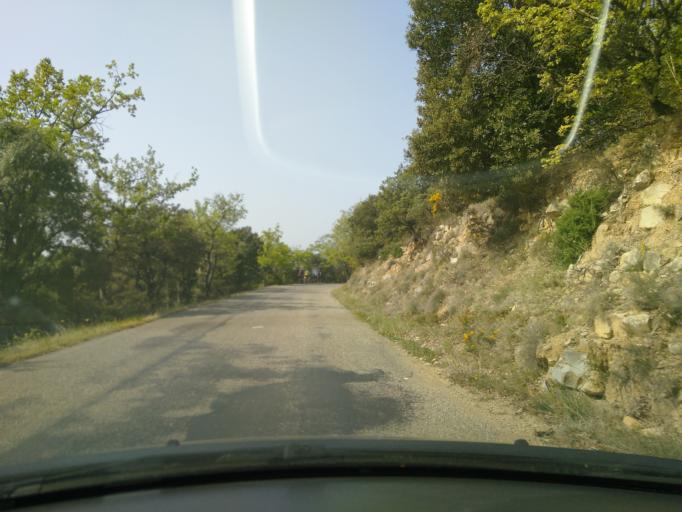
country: FR
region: Rhone-Alpes
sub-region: Departement de l'Ardeche
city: Ruoms
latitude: 44.4497
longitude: 4.3738
